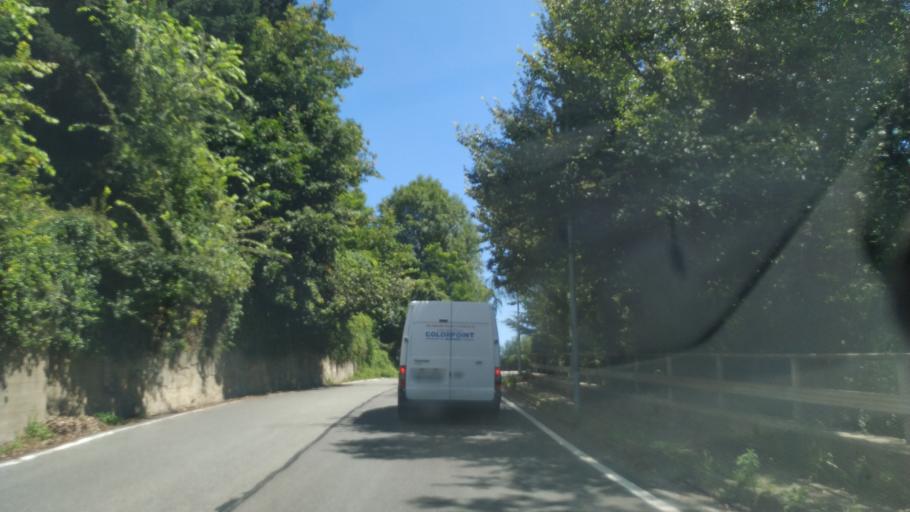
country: IT
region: Piedmont
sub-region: Provincia di Torino
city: San Mauro Torinese
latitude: 45.0772
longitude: 7.7661
